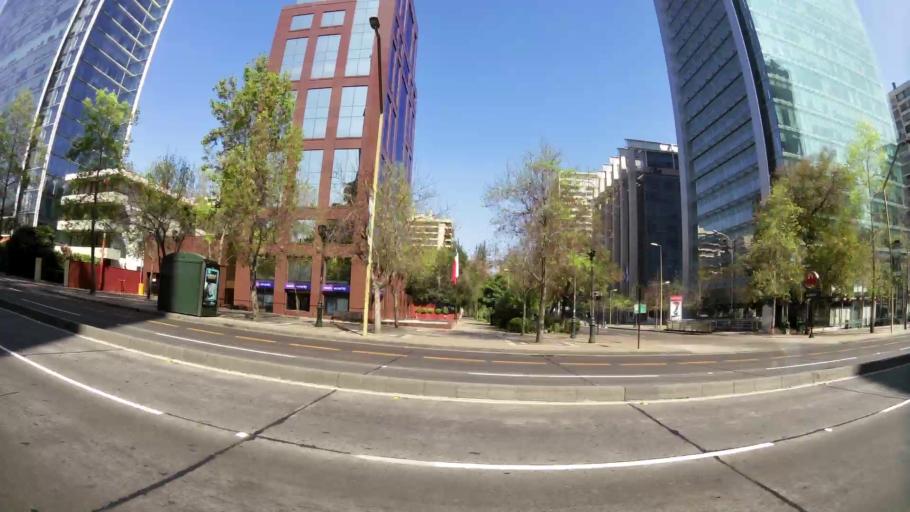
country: CL
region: Santiago Metropolitan
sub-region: Provincia de Santiago
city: Villa Presidente Frei, Nunoa, Santiago, Chile
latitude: -33.4154
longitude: -70.5896
